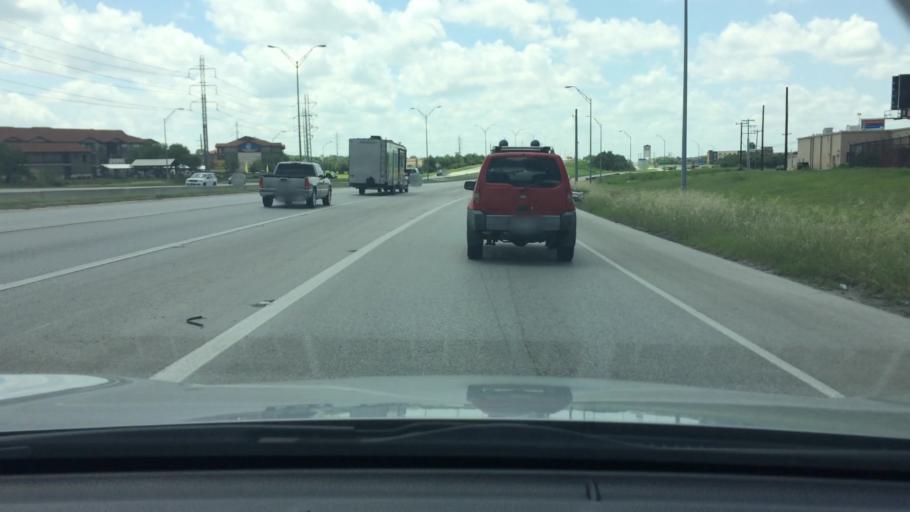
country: US
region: Texas
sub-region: Bexar County
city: China Grove
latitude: 29.3571
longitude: -98.4312
